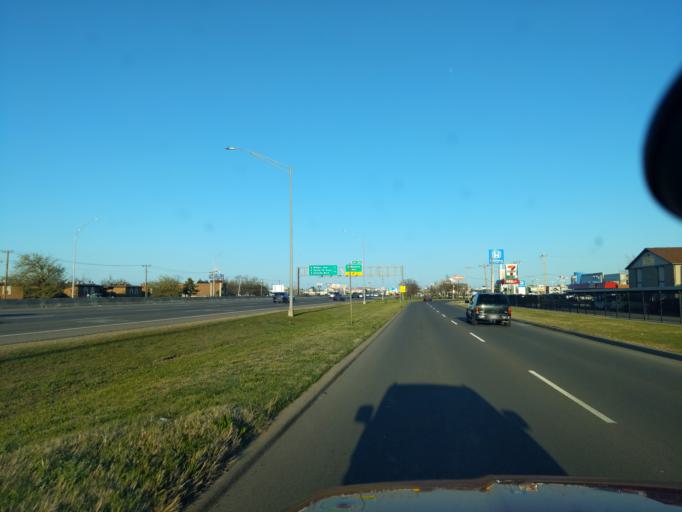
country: US
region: Oklahoma
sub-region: Cleveland County
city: Moore
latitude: 35.3912
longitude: -97.5366
